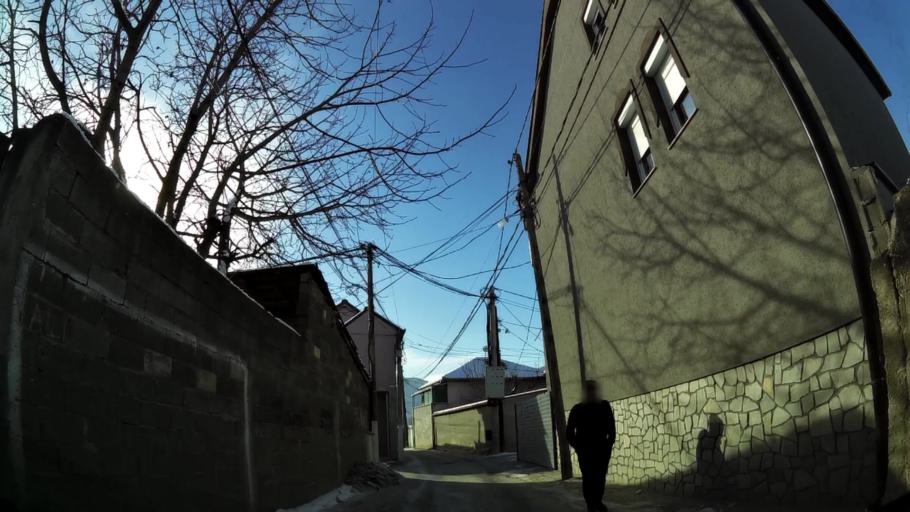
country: MK
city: Grchec
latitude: 41.9917
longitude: 21.3257
